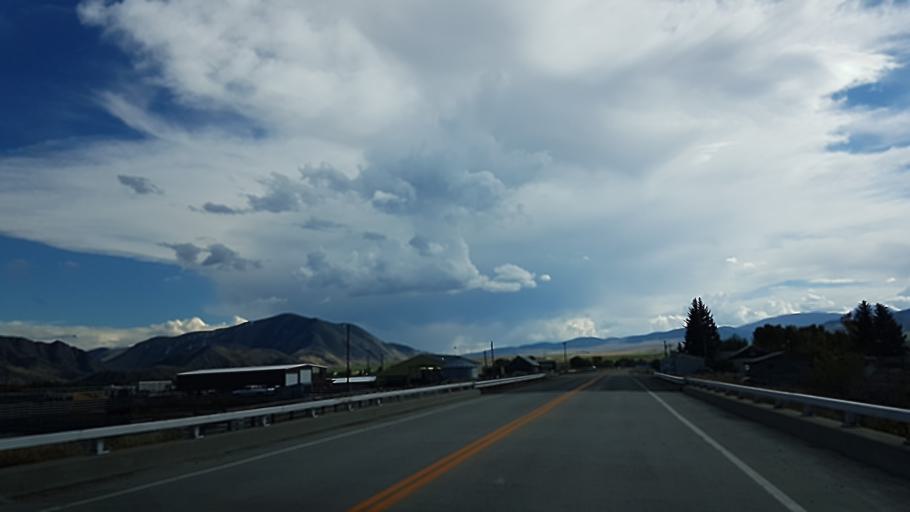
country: US
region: Montana
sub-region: Jefferson County
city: Whitehall
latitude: 45.8685
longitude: -111.9544
